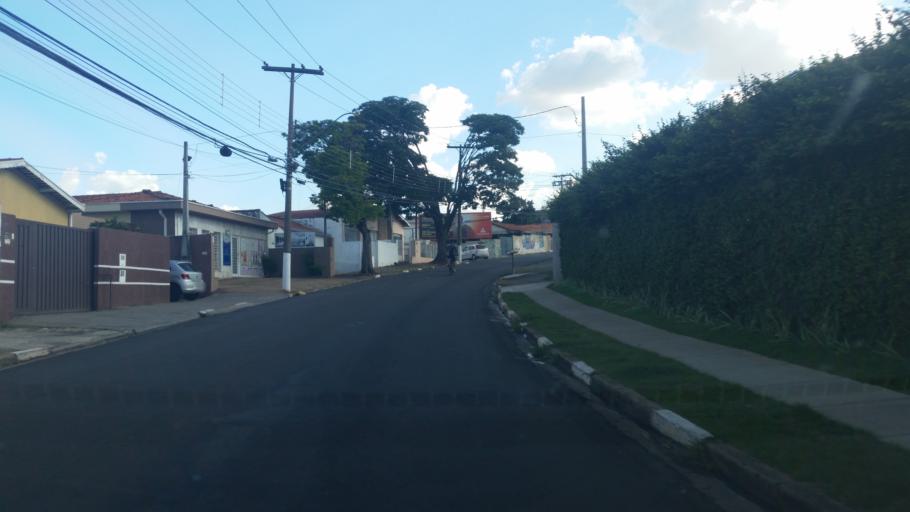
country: BR
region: Sao Paulo
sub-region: Campinas
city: Campinas
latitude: -22.8748
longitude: -47.0385
